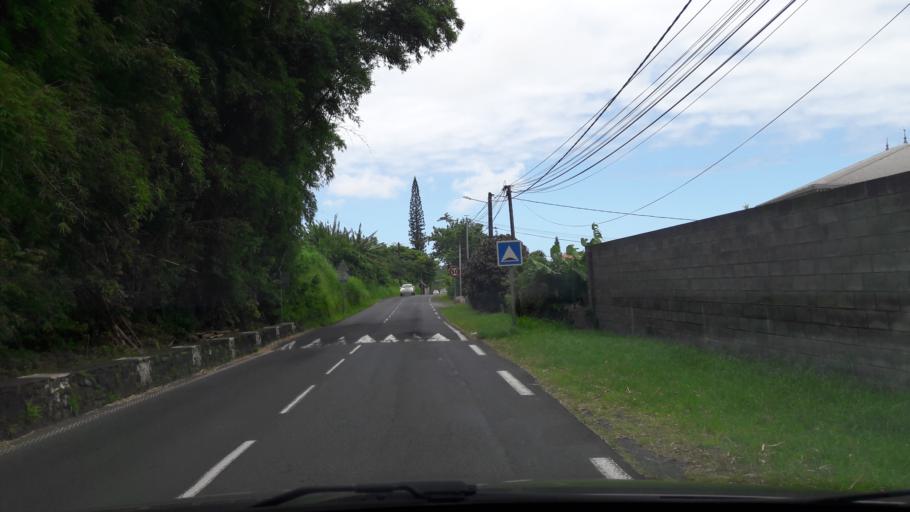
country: RE
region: Reunion
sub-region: Reunion
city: Saint-Andre
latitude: -20.9840
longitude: 55.6273
